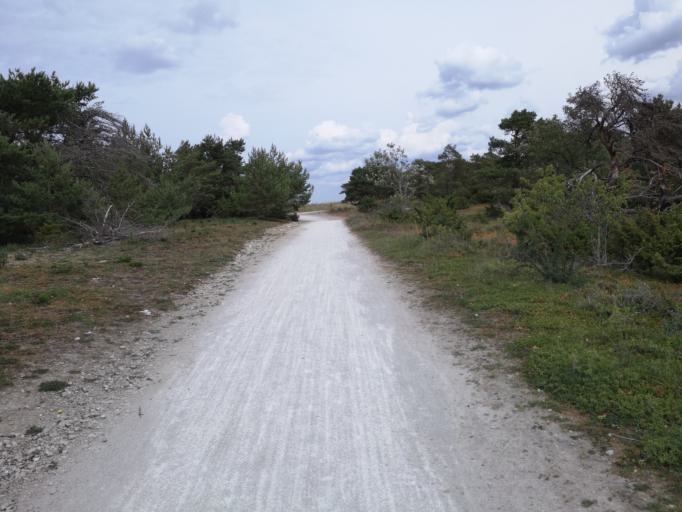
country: SE
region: Gotland
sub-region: Gotland
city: Vibble
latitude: 57.6161
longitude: 18.2606
